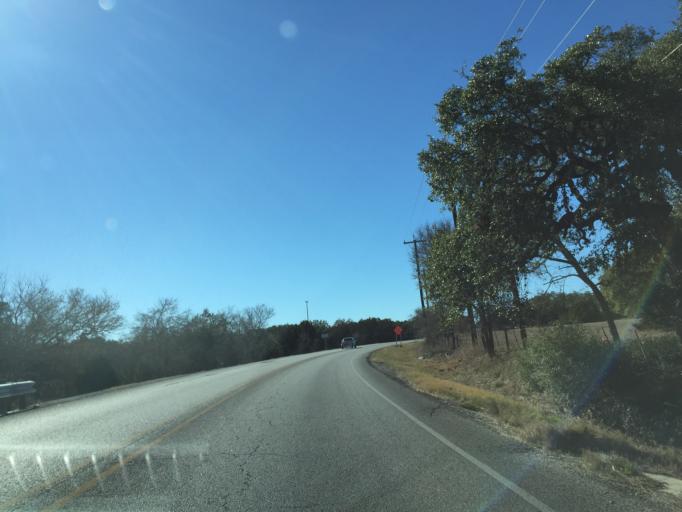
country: US
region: Texas
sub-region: Comal County
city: Bulverde
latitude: 29.7430
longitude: -98.4268
